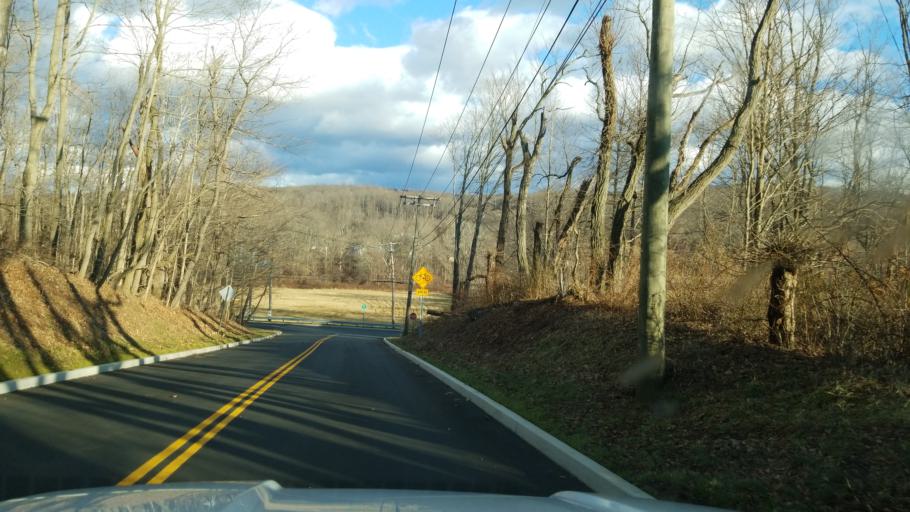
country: US
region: Connecticut
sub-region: Middlesex County
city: Middletown
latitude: 41.5128
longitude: -72.6356
